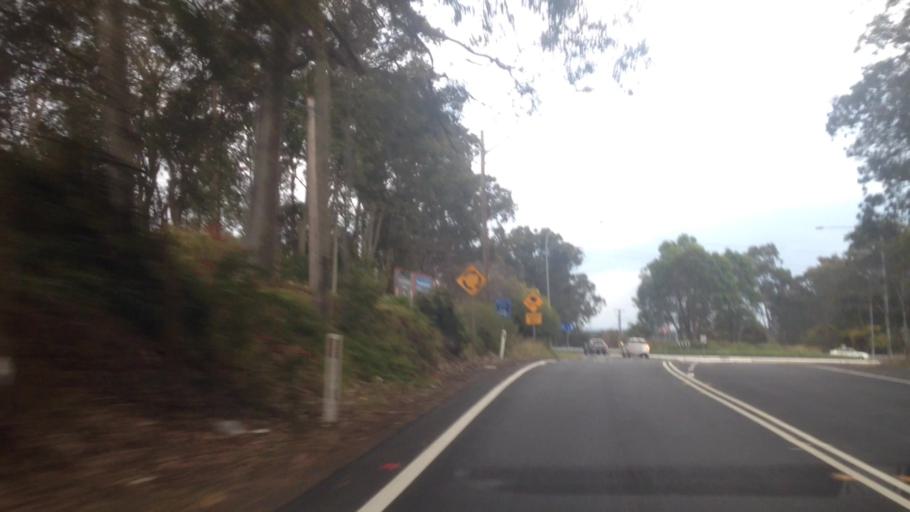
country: AU
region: New South Wales
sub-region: Wyong Shire
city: Jilliby
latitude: -33.2689
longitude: 151.4316
